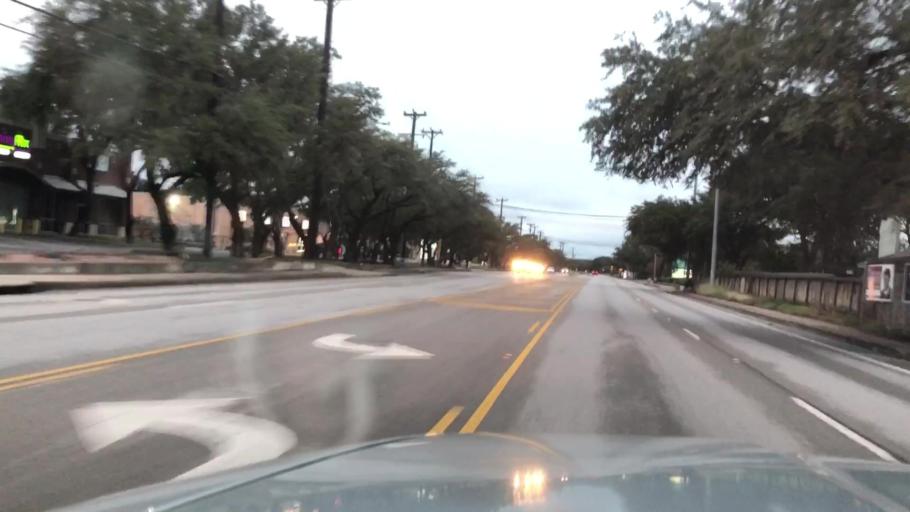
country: US
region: Texas
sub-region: Bexar County
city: Shavano Park
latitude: 29.5631
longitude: -98.6090
